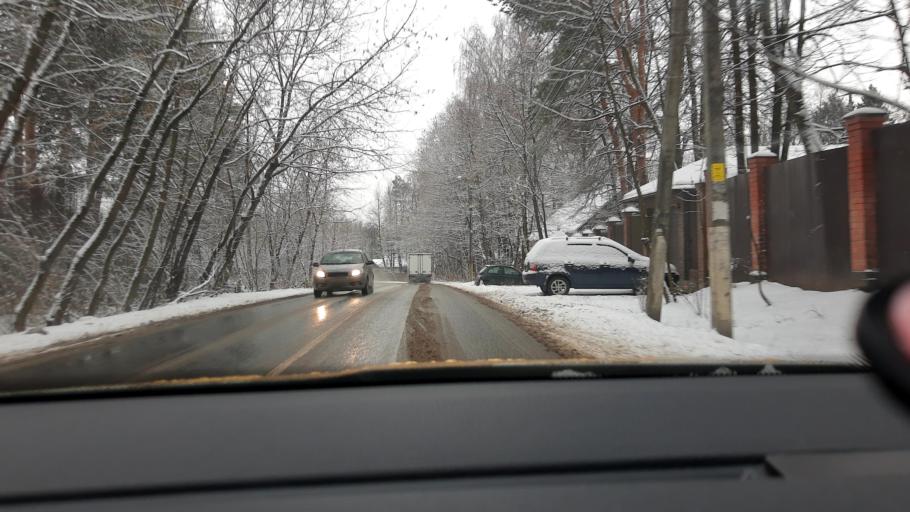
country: RU
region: Moskovskaya
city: Mamontovka
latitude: 55.9677
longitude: 37.8324
